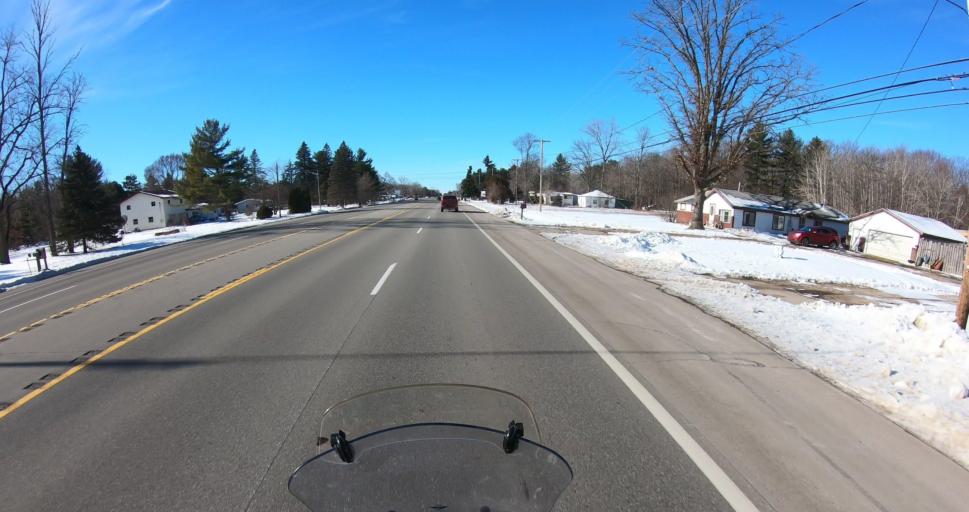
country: US
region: Michigan
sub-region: Isabella County
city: Shepherd
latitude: 43.6123
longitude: -84.6435
